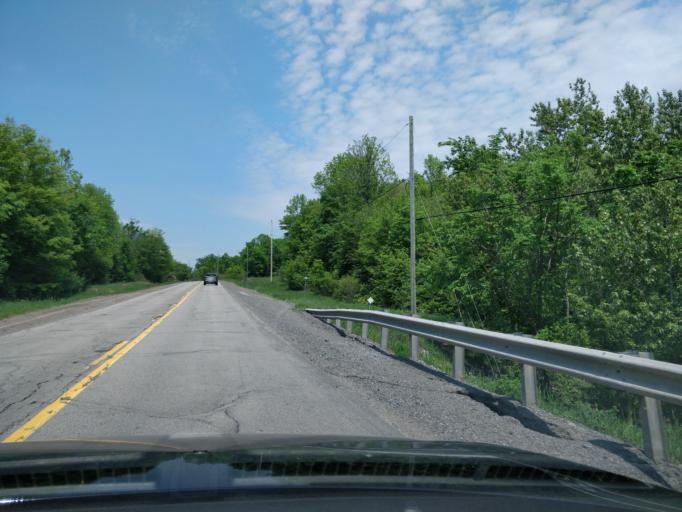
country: CA
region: Ontario
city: Perth
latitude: 44.7403
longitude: -76.3908
